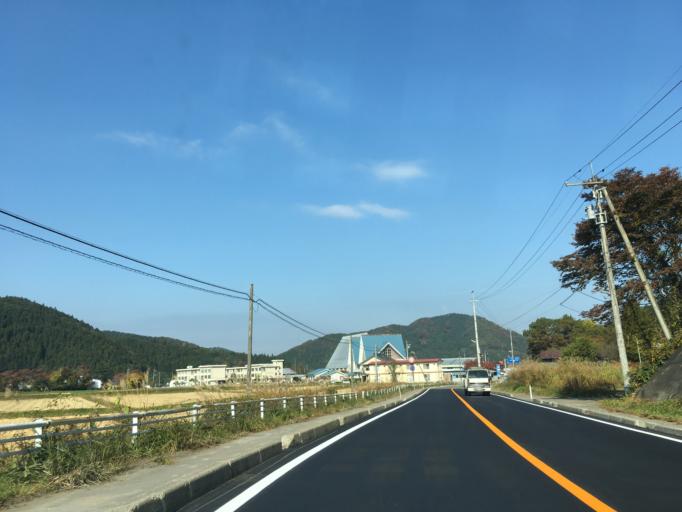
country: JP
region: Fukushima
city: Inawashiro
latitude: 37.3868
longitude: 140.0912
